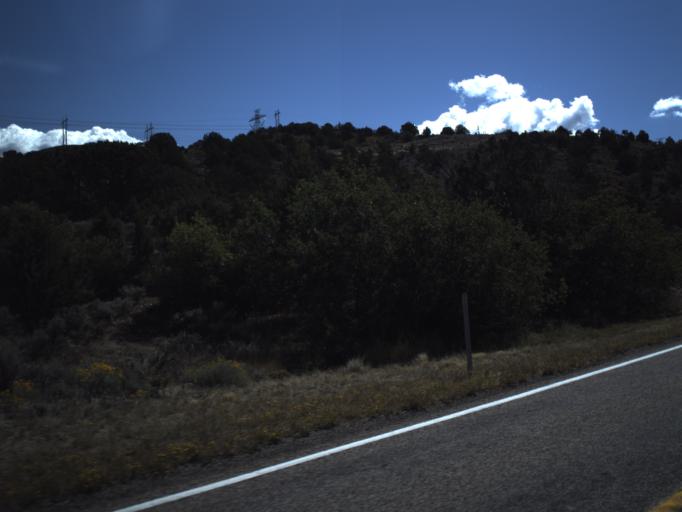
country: US
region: Utah
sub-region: Washington County
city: Enterprise
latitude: 37.4775
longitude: -113.6280
